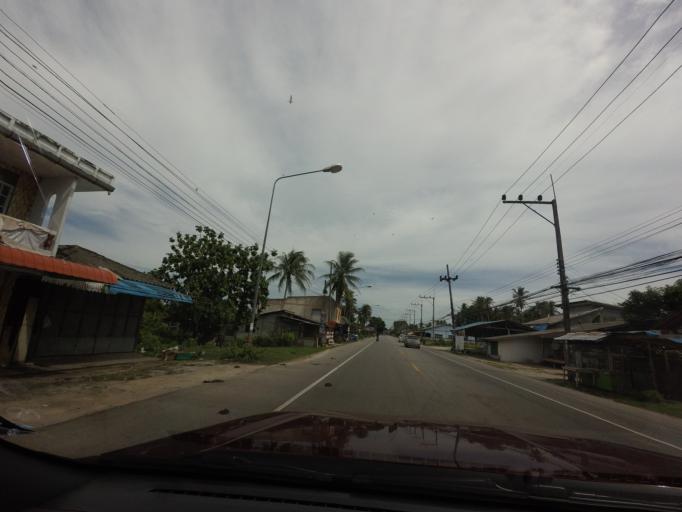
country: TH
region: Narathiwat
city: Tak Bai
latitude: 6.2472
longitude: 102.0709
